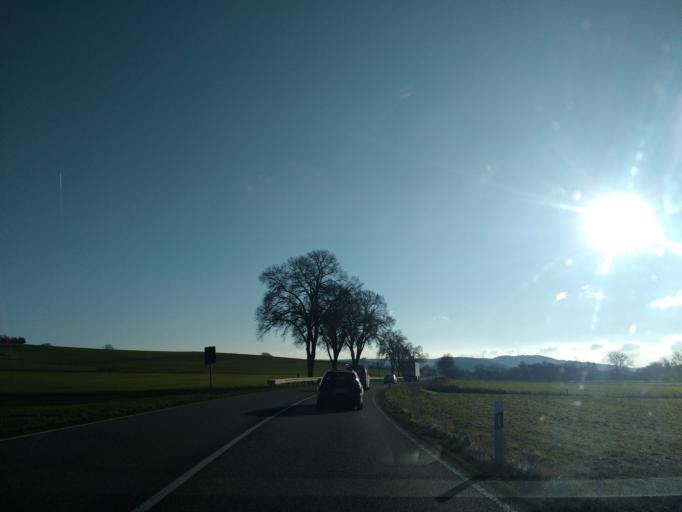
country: DE
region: Hesse
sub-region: Regierungsbezirk Kassel
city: Schrecksbach
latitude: 50.8682
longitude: 9.2782
